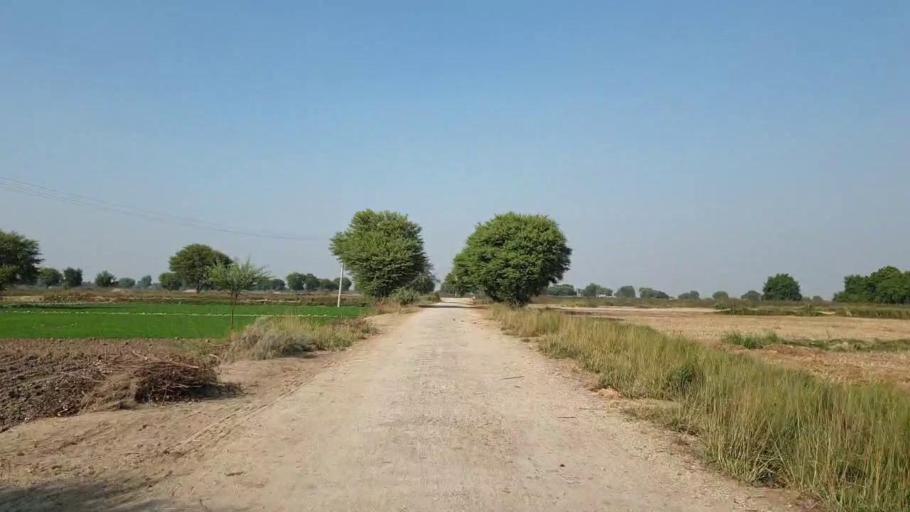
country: PK
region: Sindh
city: Sehwan
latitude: 26.4564
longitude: 67.8158
